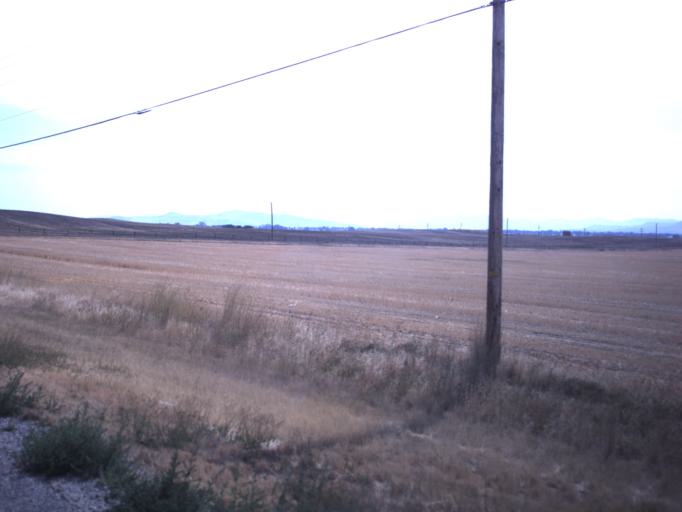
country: US
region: Utah
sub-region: Box Elder County
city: Garland
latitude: 41.7544
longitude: -112.0985
